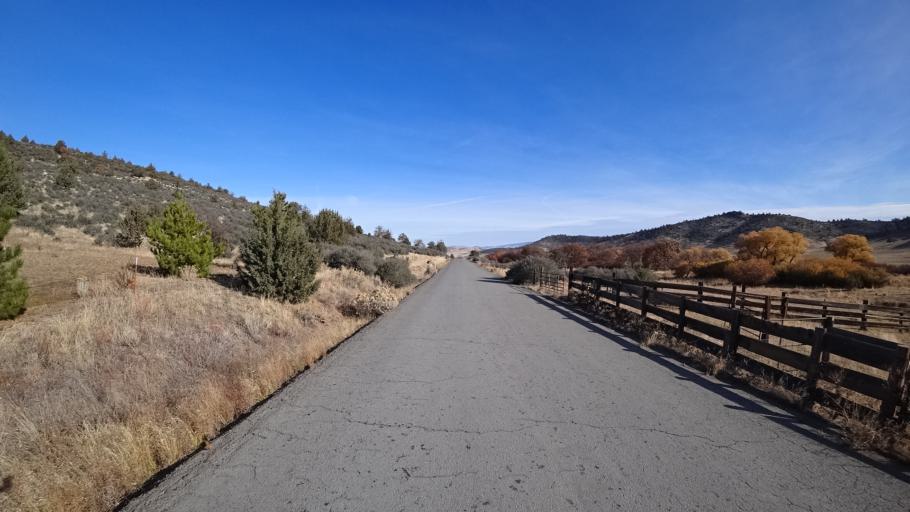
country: US
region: California
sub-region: Siskiyou County
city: Montague
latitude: 41.6277
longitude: -122.5719
